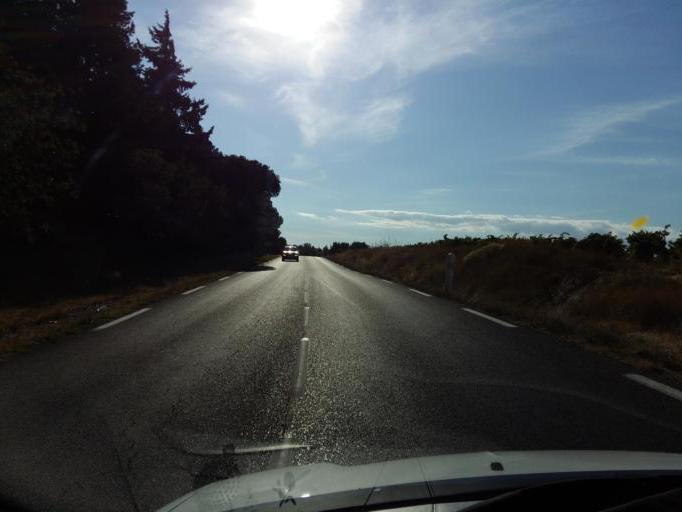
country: FR
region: Provence-Alpes-Cote d'Azur
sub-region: Departement du Vaucluse
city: Jonquerettes
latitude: 43.9321
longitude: 4.9269
